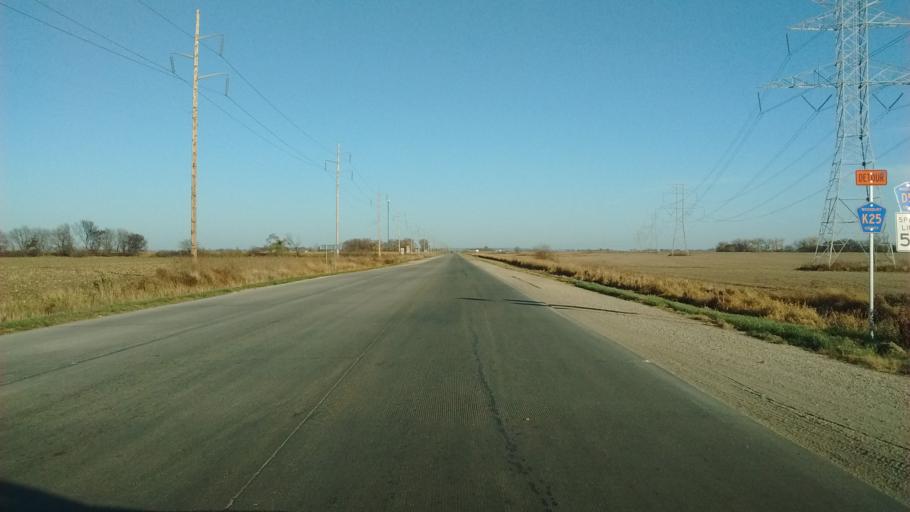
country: US
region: Iowa
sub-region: Woodbury County
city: Sergeant Bluff
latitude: 42.3301
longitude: -96.3492
